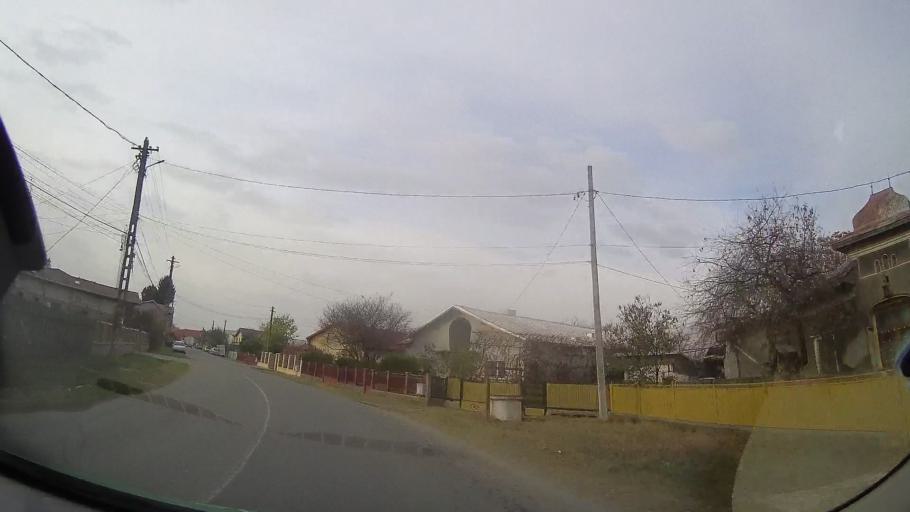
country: RO
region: Prahova
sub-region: Comuna Gorgota
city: Potigrafu
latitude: 44.7843
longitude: 26.1010
